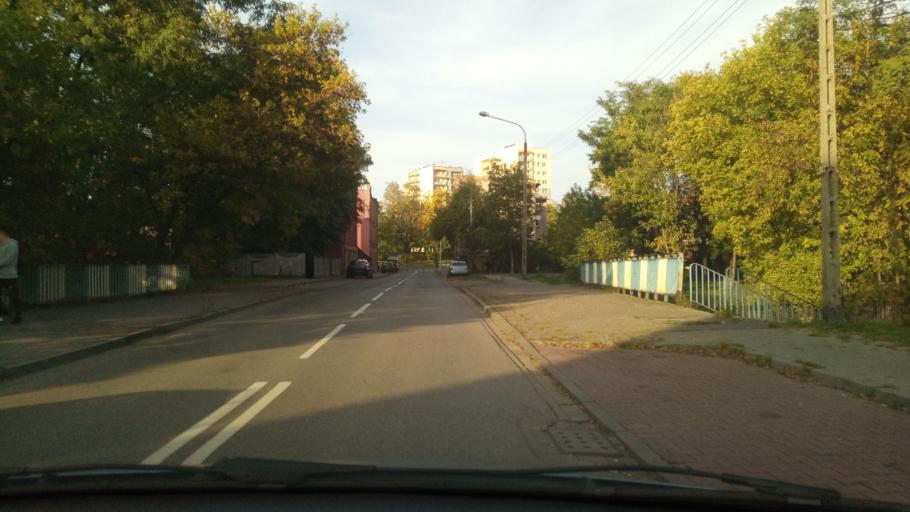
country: PL
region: Silesian Voivodeship
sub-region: Sosnowiec
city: Sosnowiec
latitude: 50.2631
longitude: 19.1042
